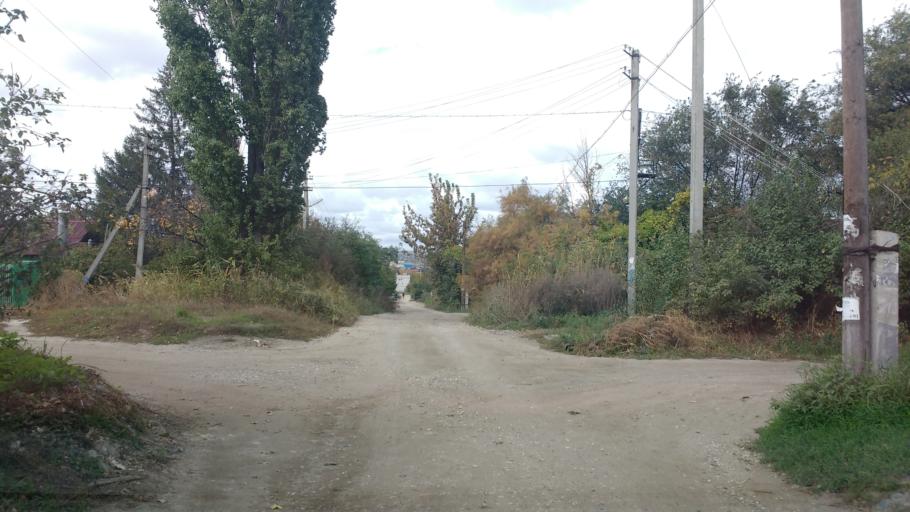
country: RU
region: Volgograd
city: Vodstroy
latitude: 48.7796
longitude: 44.5404
